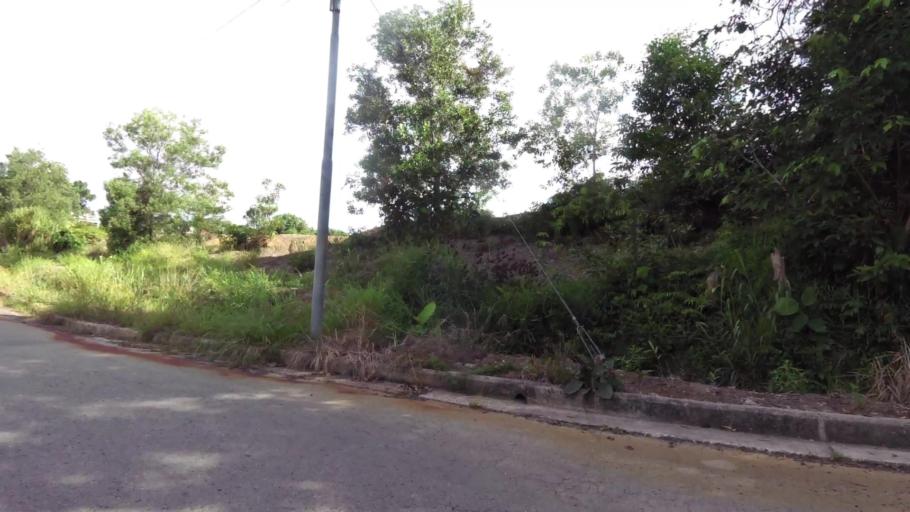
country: BN
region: Brunei and Muara
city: Bandar Seri Begawan
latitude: 5.0136
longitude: 115.0328
